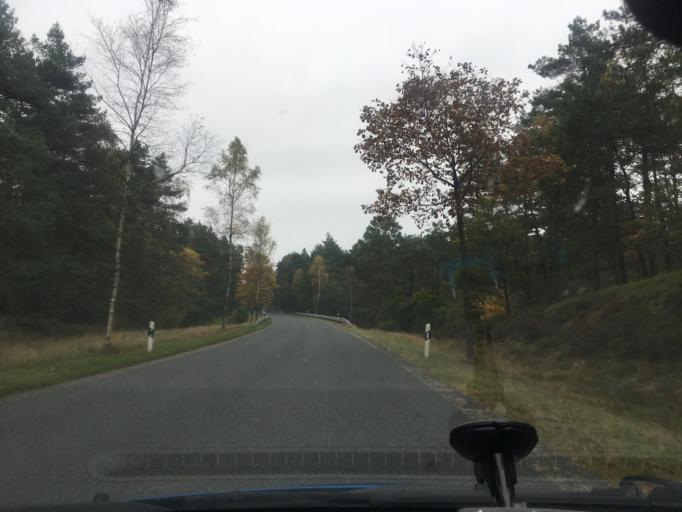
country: DE
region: Lower Saxony
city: Bispingen
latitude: 53.0960
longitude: 10.0563
